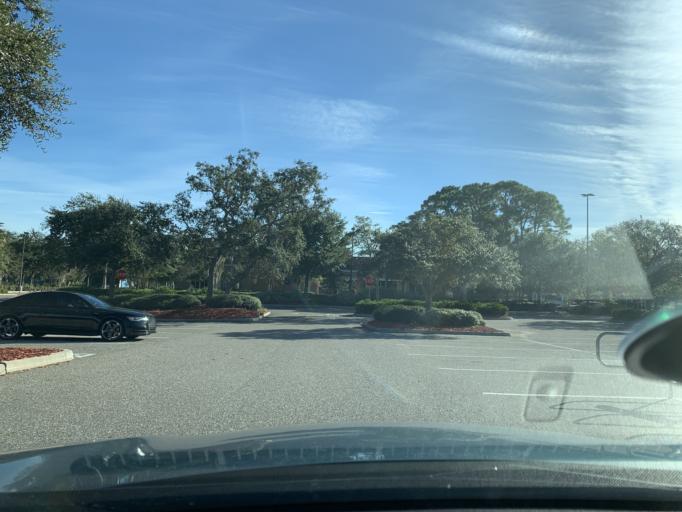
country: US
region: Florida
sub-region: Pinellas County
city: Gulfport
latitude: 27.7367
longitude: -82.6809
